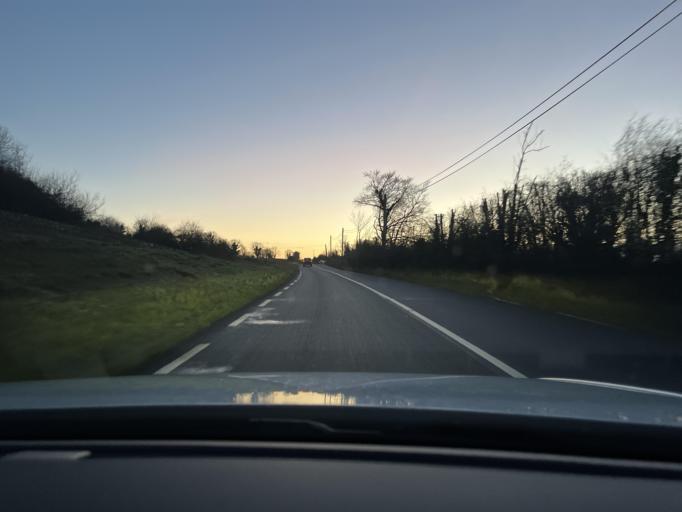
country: IE
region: Connaught
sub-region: County Leitrim
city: Carrick-on-Shannon
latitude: 53.9999
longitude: -8.0262
